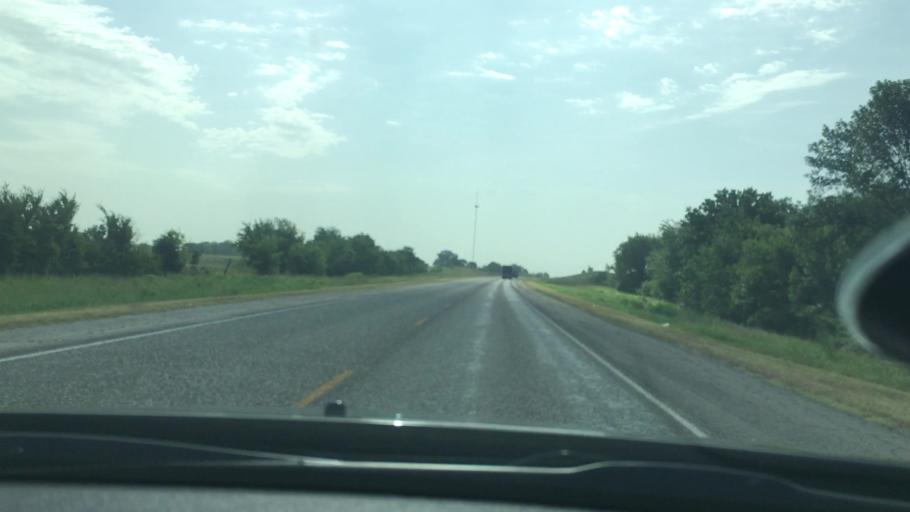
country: US
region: Oklahoma
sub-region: Coal County
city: Coalgate
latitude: 34.5997
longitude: -96.3230
